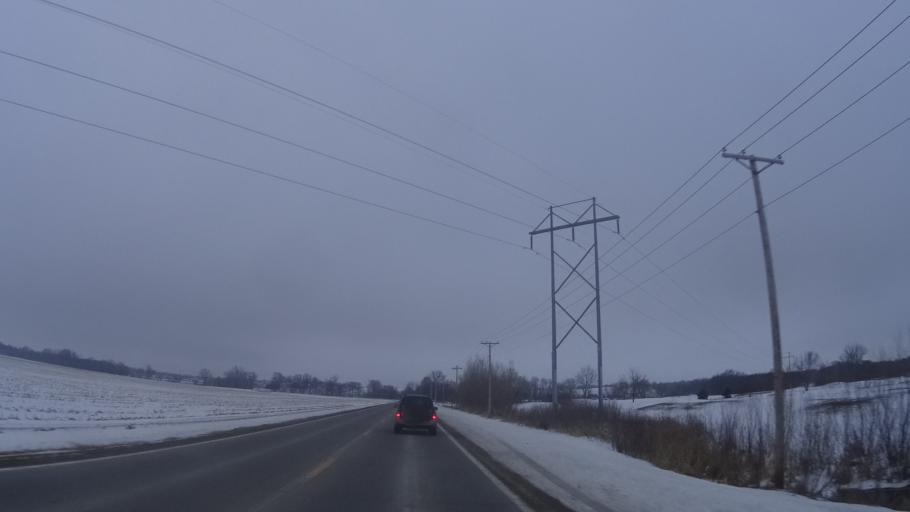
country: US
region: Nebraska
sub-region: Sarpy County
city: La Vista
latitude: 41.1594
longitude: -95.9886
